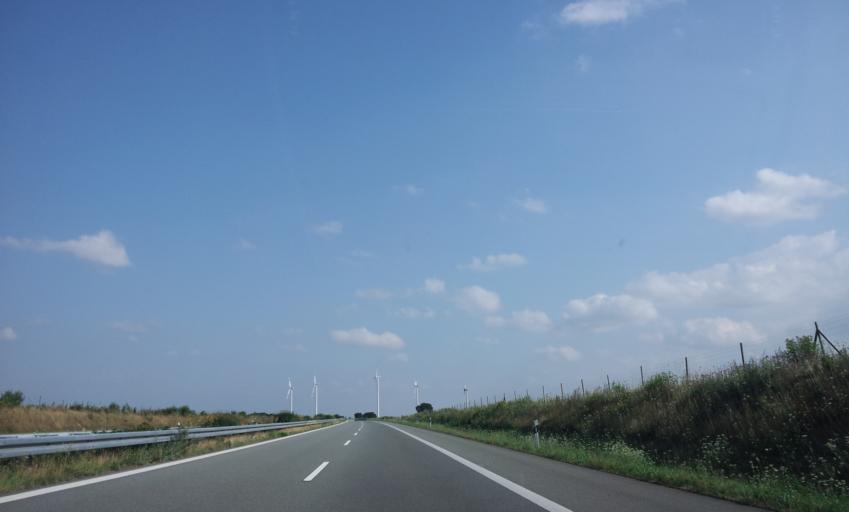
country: DE
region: Mecklenburg-Vorpommern
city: Gormin
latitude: 54.0133
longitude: 13.2901
